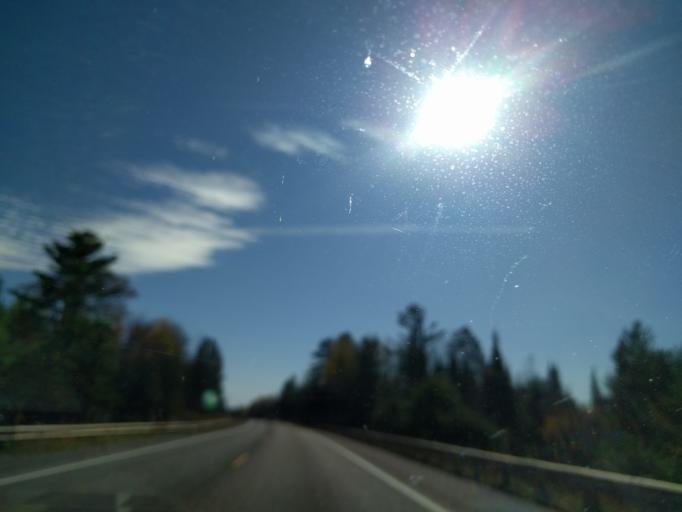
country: US
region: Michigan
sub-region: Marquette County
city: West Ishpeming
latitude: 46.4022
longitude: -87.9982
